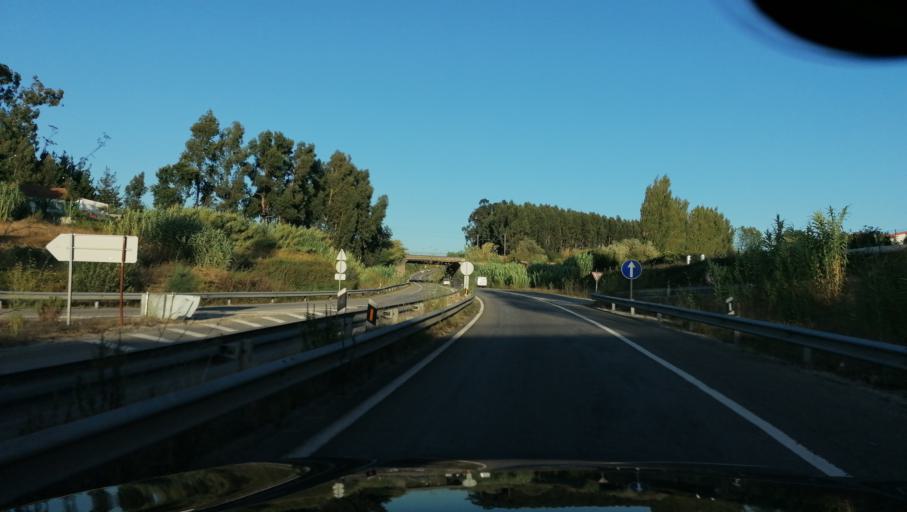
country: PT
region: Aveiro
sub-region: Aveiro
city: Aradas
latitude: 40.6112
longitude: -8.6309
